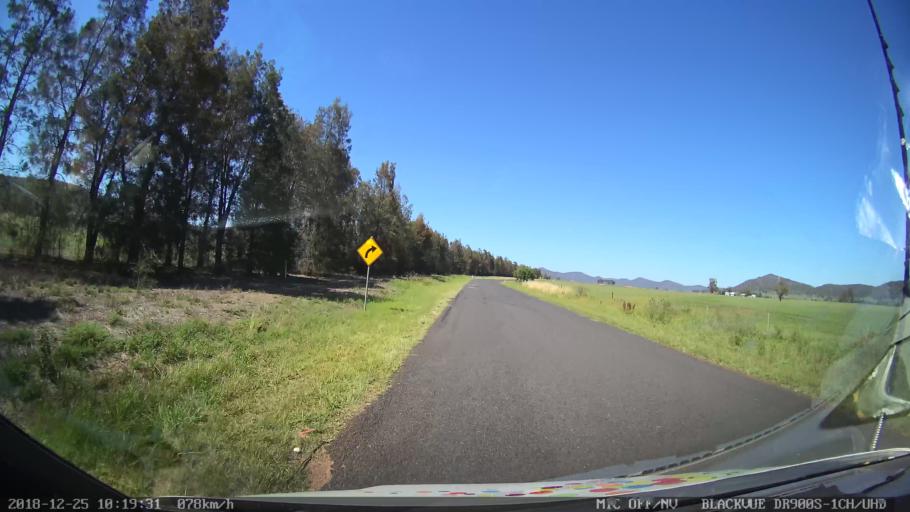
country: AU
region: New South Wales
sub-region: Muswellbrook
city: Denman
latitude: -32.3515
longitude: 150.5578
